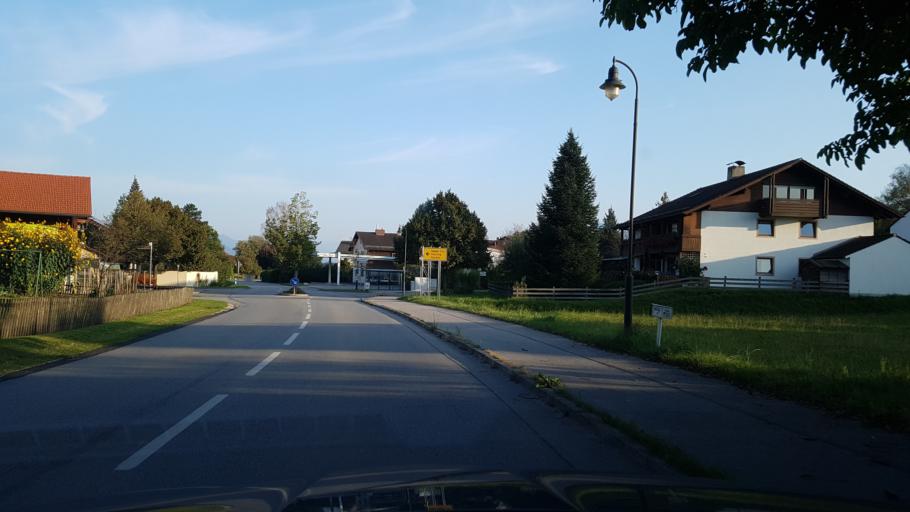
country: DE
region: Bavaria
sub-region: Upper Bavaria
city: Ainring
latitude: 47.8712
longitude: 12.9289
